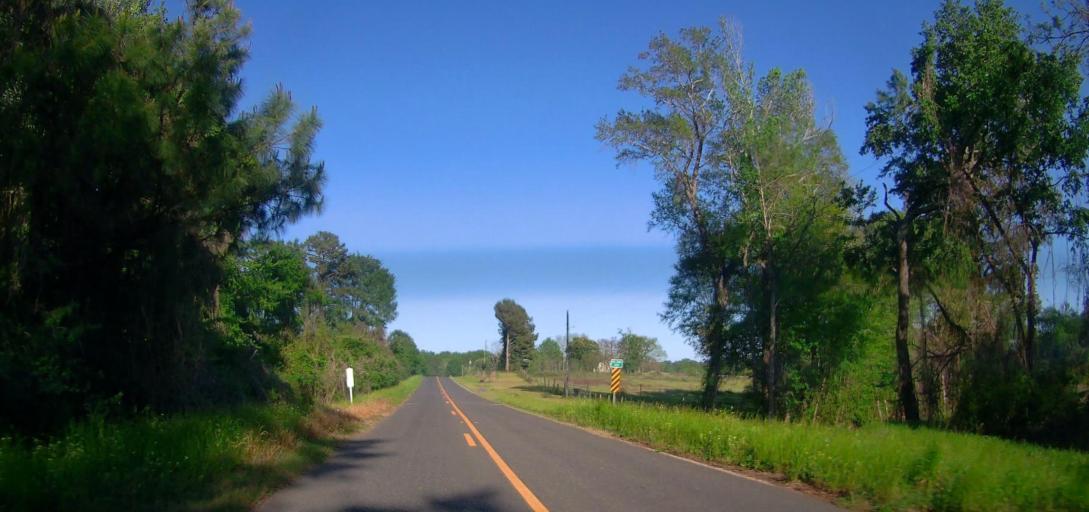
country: US
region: Georgia
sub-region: Macon County
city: Marshallville
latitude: 32.3825
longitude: -83.8701
